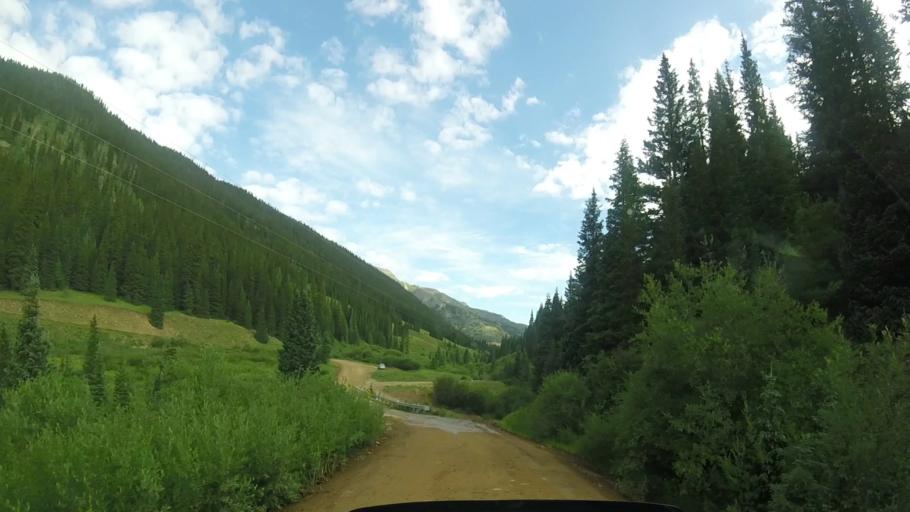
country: US
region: Colorado
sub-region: San Juan County
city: Silverton
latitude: 37.8503
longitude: -107.7260
